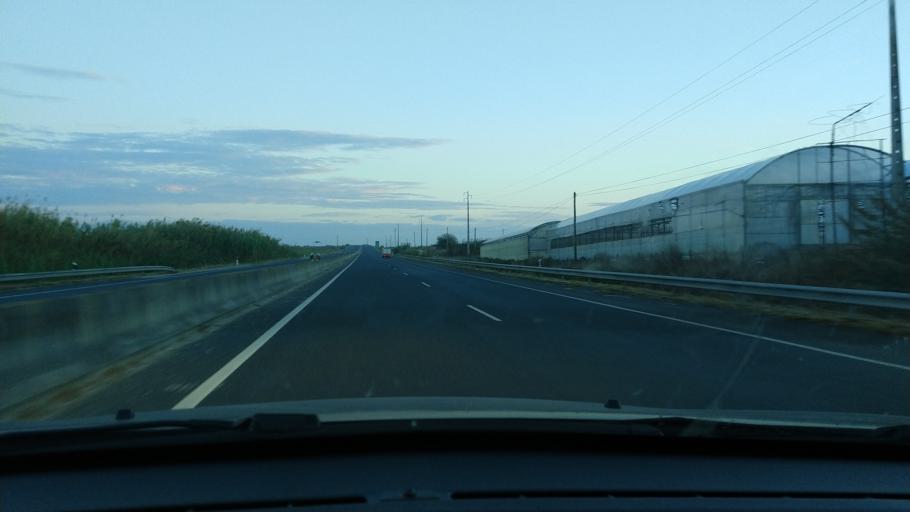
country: PT
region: Leiria
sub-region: Peniche
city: Atouguia da Baleia
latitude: 39.3410
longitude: -9.3388
